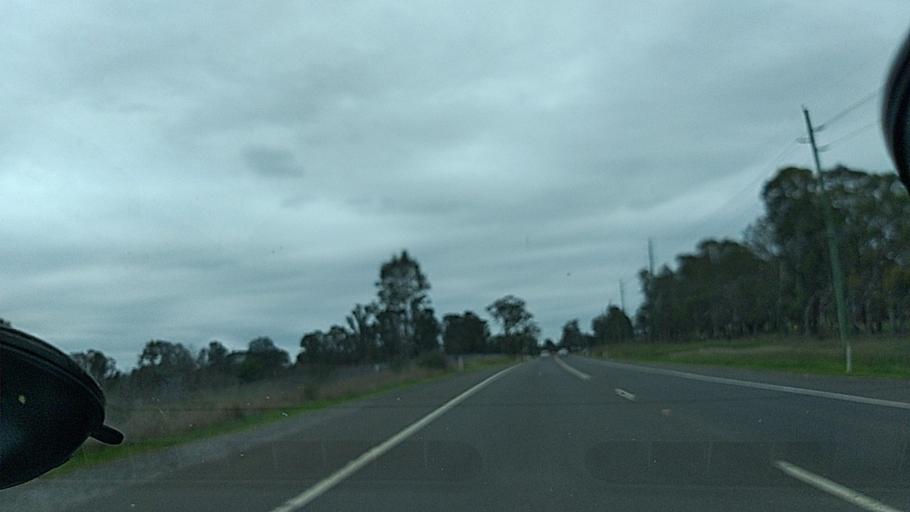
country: AU
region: New South Wales
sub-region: Penrith Municipality
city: Glenmore Park
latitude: -33.8013
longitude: 150.6973
